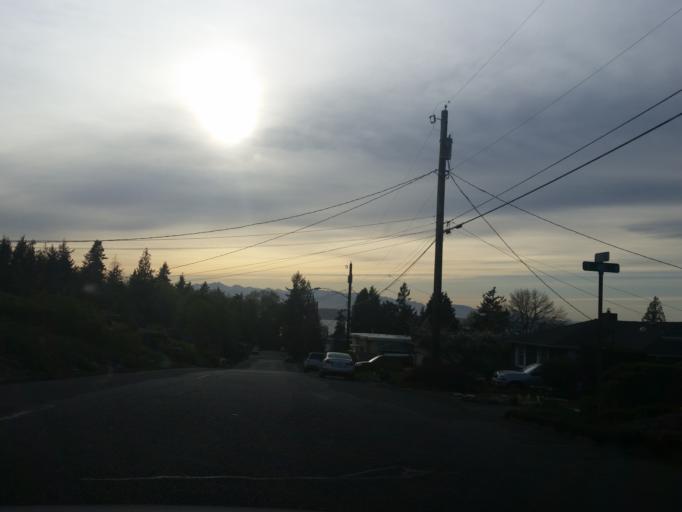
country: US
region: Washington
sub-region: Snohomish County
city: Edmonds
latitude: 47.8129
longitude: -122.3642
